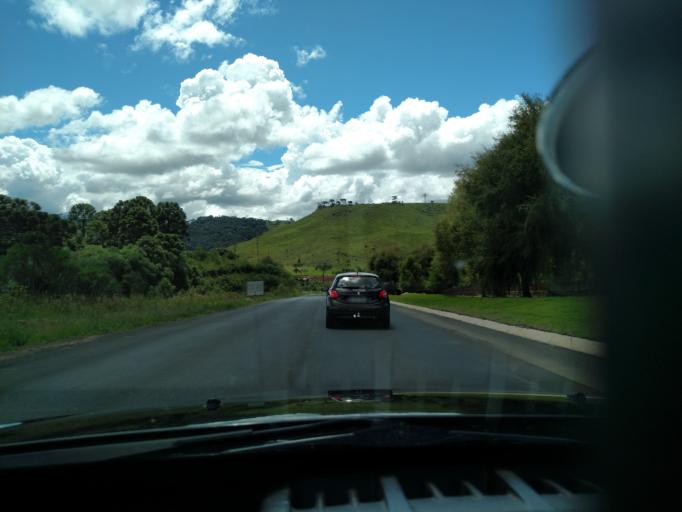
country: BR
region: Santa Catarina
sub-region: Sao Joaquim
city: Sao Joaquim
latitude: -28.2590
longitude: -49.9636
